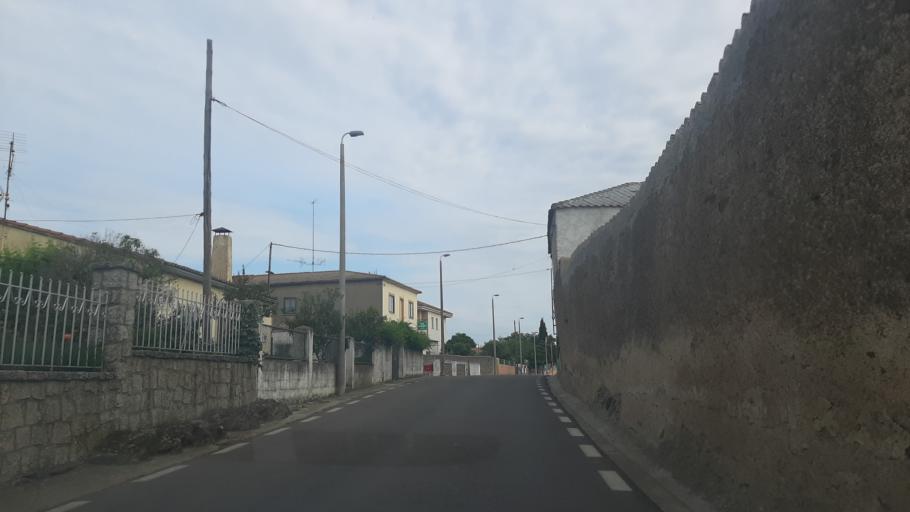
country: ES
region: Castille and Leon
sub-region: Provincia de Salamanca
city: Gallegos de Arganan
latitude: 40.6306
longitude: -6.7046
